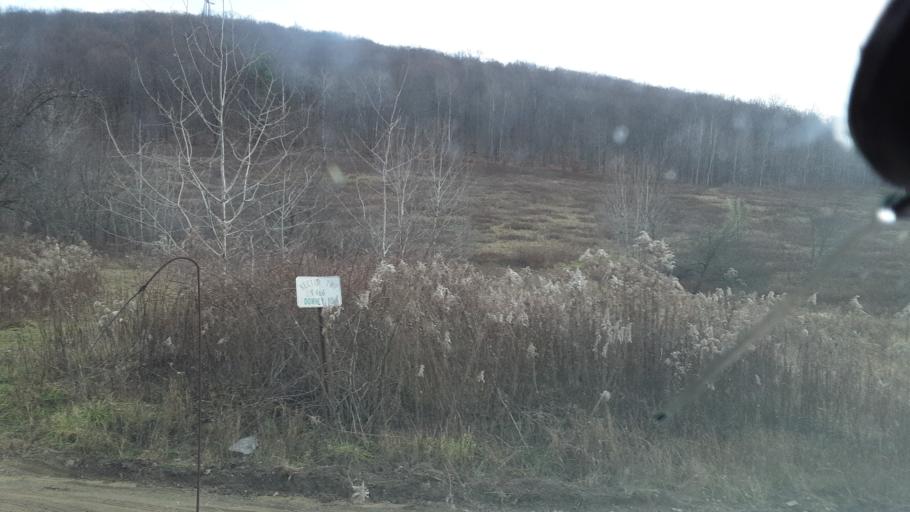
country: US
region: Pennsylvania
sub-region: Tioga County
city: Westfield
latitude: 41.9030
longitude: -77.7142
